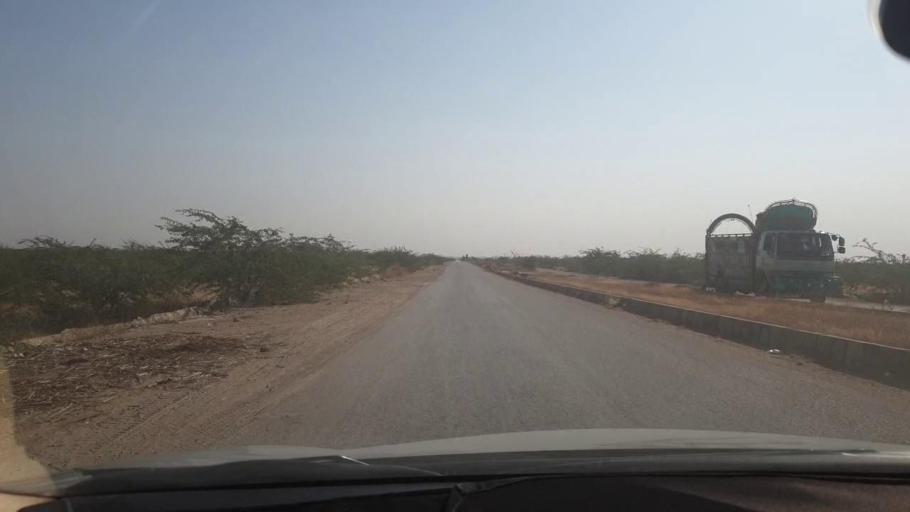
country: PK
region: Sindh
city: Malir Cantonment
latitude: 25.0759
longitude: 67.1384
